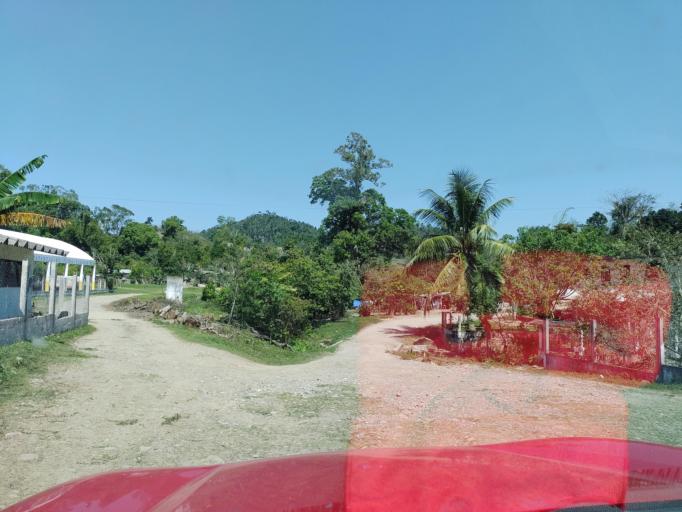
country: MX
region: Veracruz
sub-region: Papantla
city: Polutla
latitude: 20.4982
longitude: -97.2325
